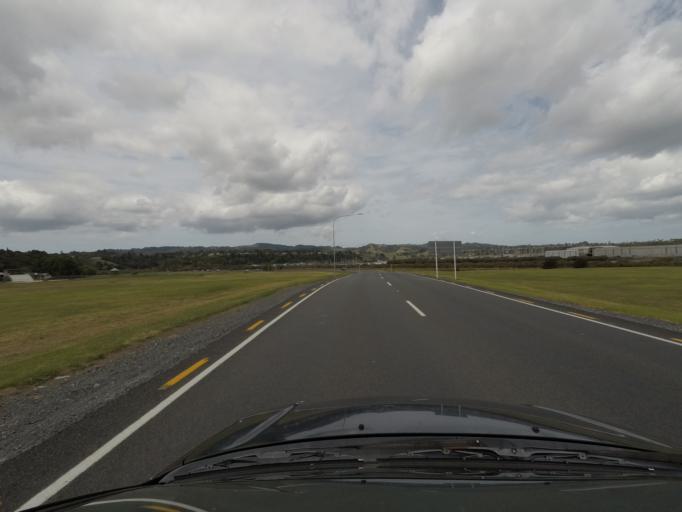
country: NZ
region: Northland
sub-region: Whangarei
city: Whangarei
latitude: -35.7348
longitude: 174.3386
